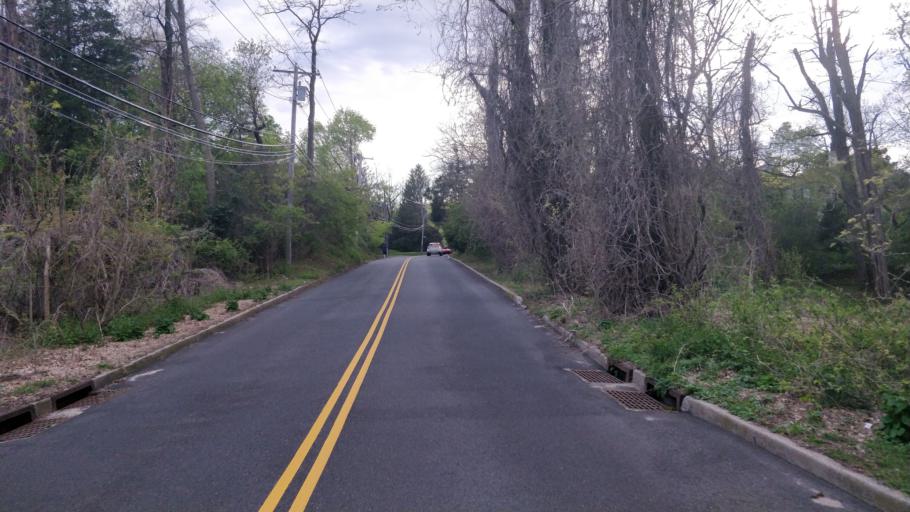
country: US
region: New York
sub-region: Suffolk County
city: Kings Park
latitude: 40.9040
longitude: -73.2705
